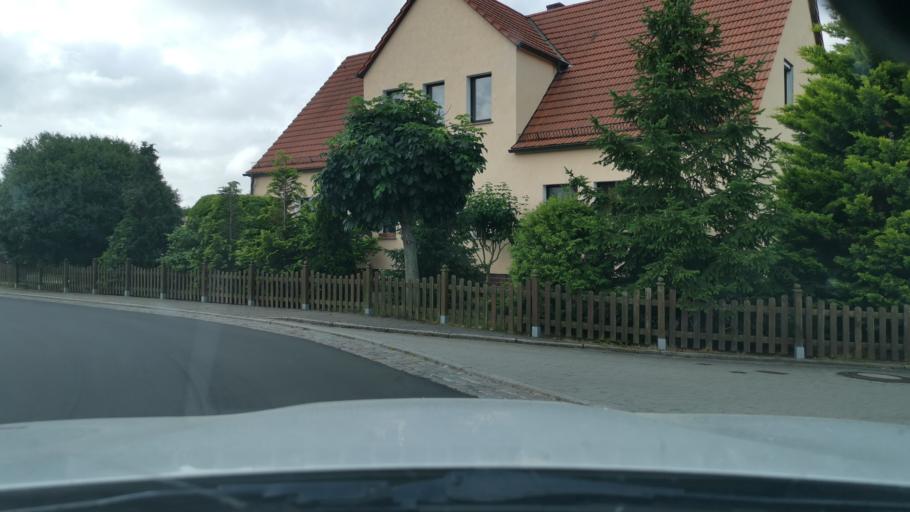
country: DE
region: Saxony
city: Torgau
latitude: 51.6054
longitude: 13.0252
